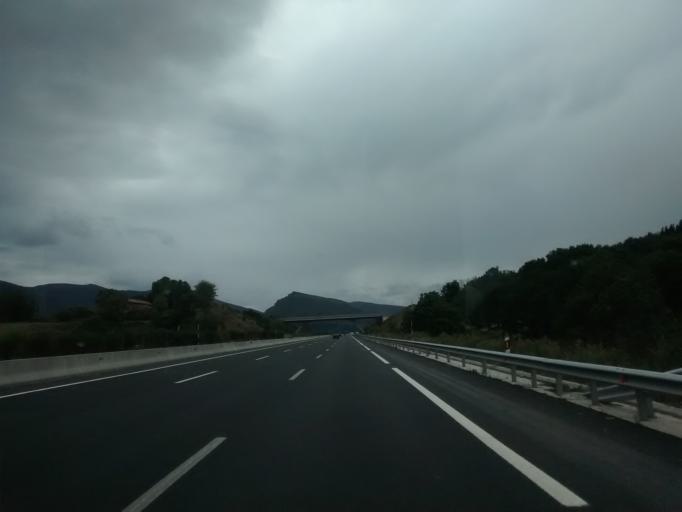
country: ES
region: Cantabria
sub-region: Provincia de Cantabria
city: Molledo
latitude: 43.1487
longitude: -4.0548
